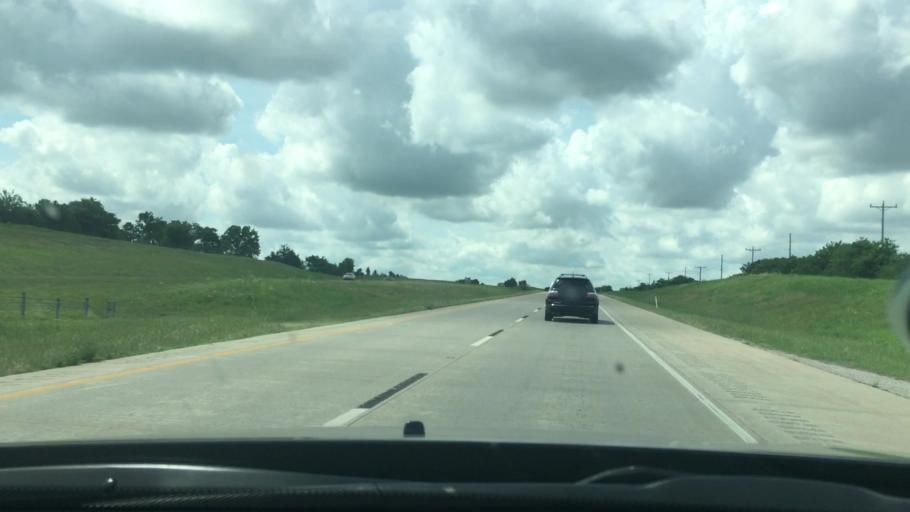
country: US
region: Oklahoma
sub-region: Love County
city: Marietta
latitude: 33.8725
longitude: -97.1344
